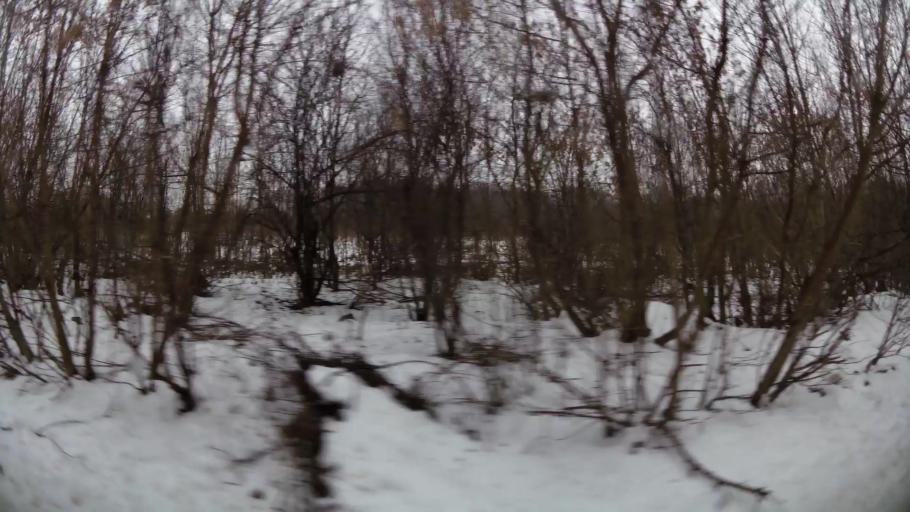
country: RO
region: Ilfov
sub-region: Comuna Mogosoaia
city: Mogosoaia
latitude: 44.5093
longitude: 26.0142
